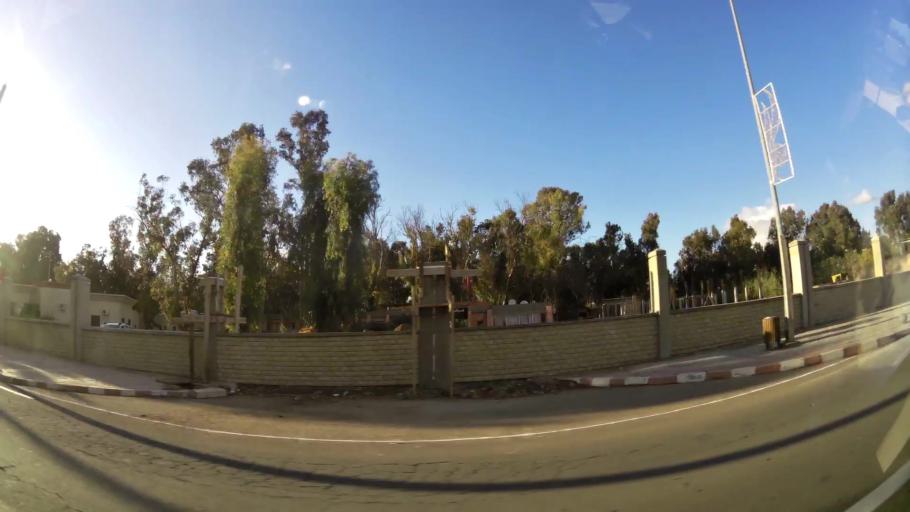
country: MA
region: Marrakech-Tensift-Al Haouz
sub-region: Kelaa-Des-Sraghna
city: Sidi Bou Othmane
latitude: 32.2290
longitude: -7.9590
